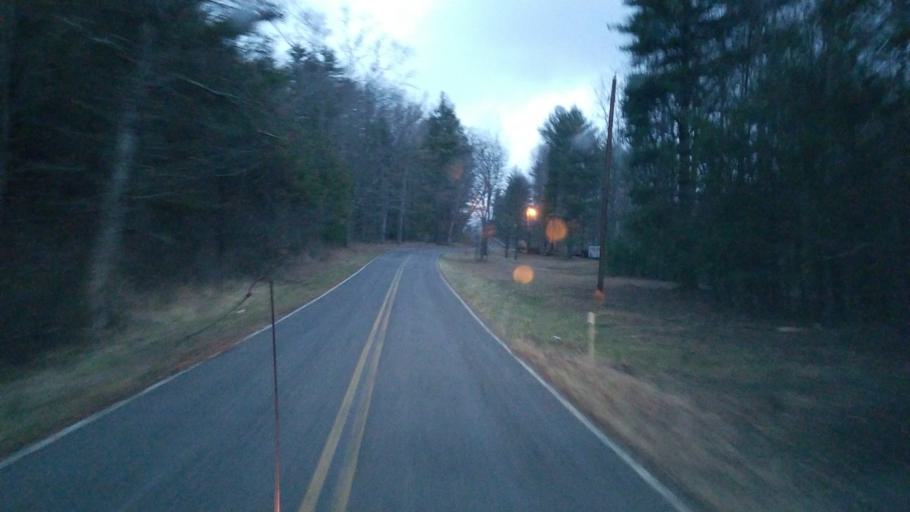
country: US
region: Virginia
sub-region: Pulaski County
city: Pulaski
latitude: 37.1175
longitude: -80.8761
